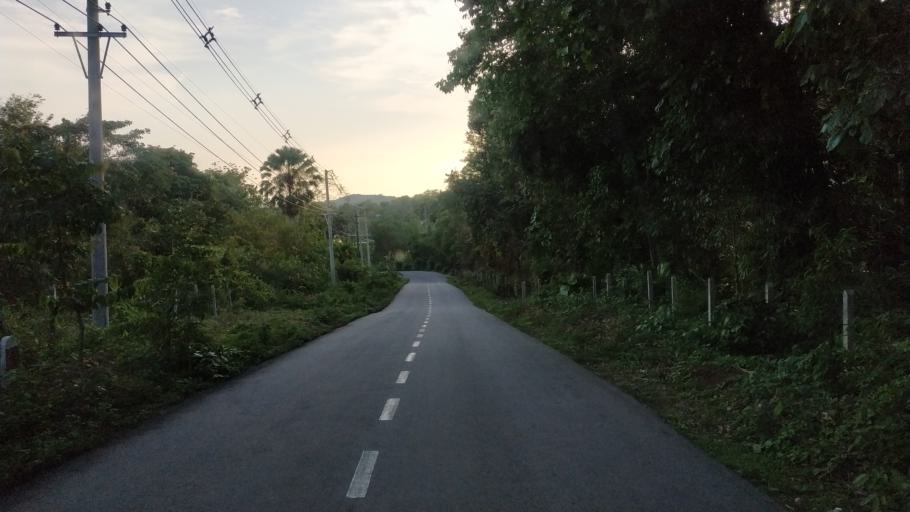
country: MM
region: Mon
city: Kyaikto
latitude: 17.4219
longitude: 97.0735
